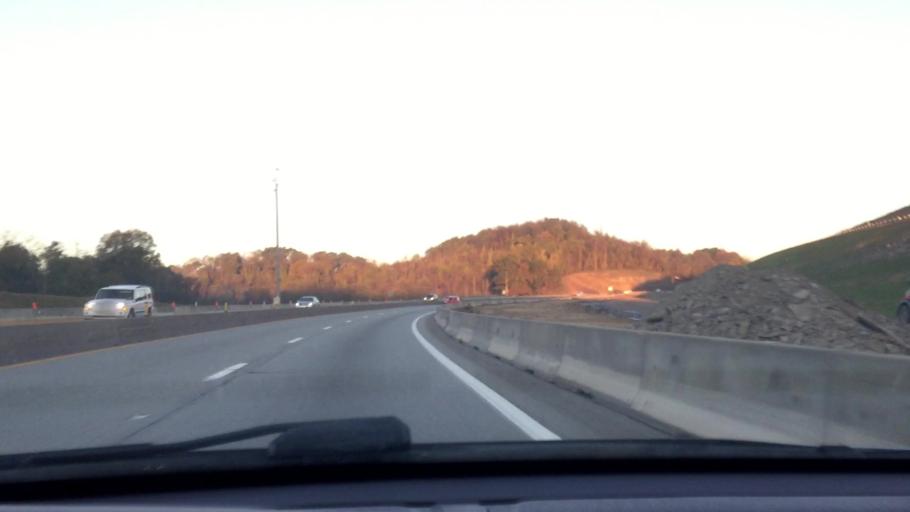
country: US
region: Pennsylvania
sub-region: Washington County
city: East Washington
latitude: 40.1574
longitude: -80.1557
